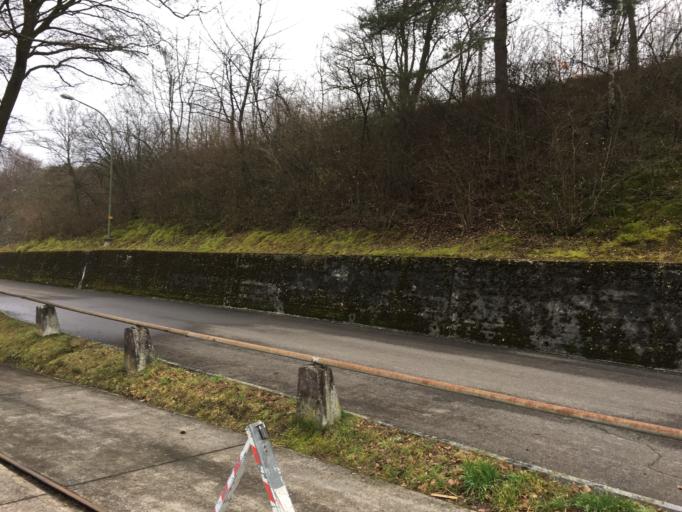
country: CH
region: Aargau
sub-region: Bezirk Zurzach
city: Bad Zurzach
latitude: 47.5698
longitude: 8.3389
